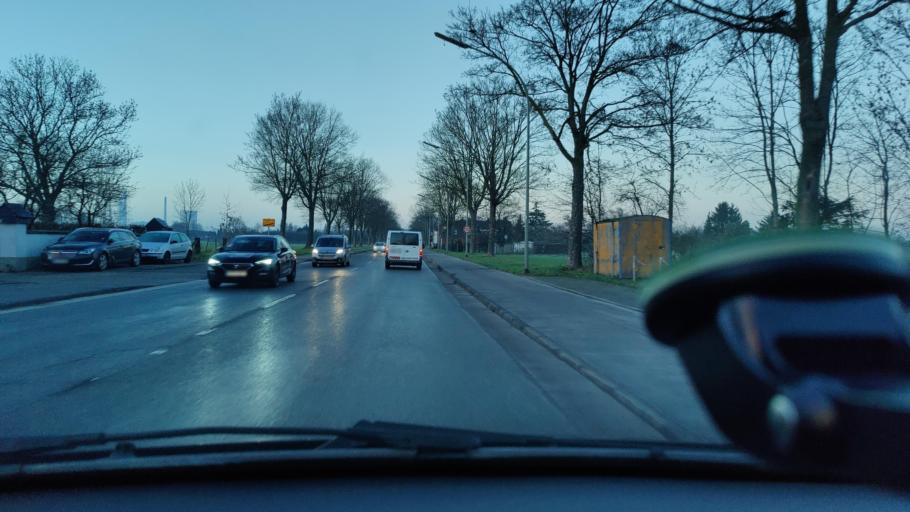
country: DE
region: North Rhine-Westphalia
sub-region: Regierungsbezirk Dusseldorf
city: Dinslaken
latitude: 51.5507
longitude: 6.7133
